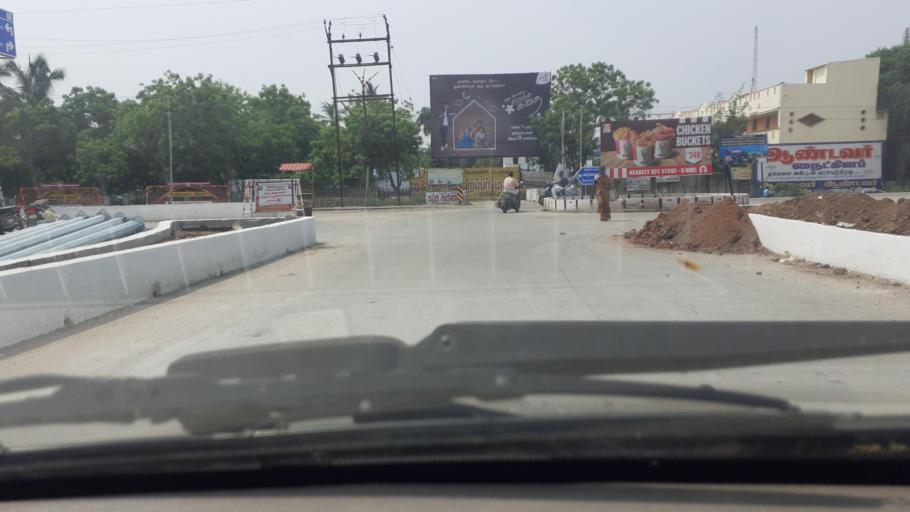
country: IN
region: Tamil Nadu
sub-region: Thoothukkudi
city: Korampallam
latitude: 8.8079
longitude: 78.1386
